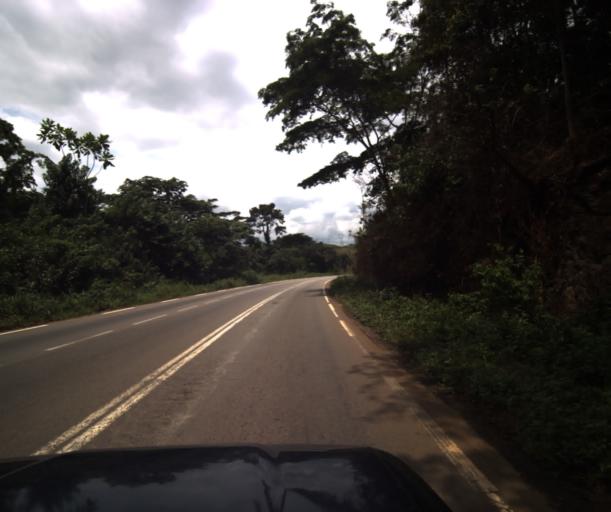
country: CM
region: Centre
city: Eseka
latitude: 3.8718
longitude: 10.8312
